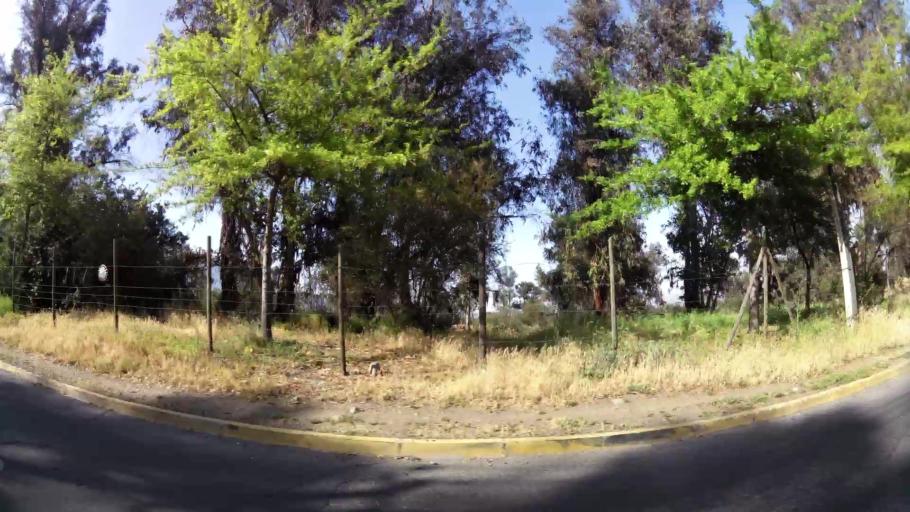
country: CL
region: Santiago Metropolitan
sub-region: Provincia de Santiago
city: Villa Presidente Frei, Nunoa, Santiago, Chile
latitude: -33.5010
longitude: -70.5378
